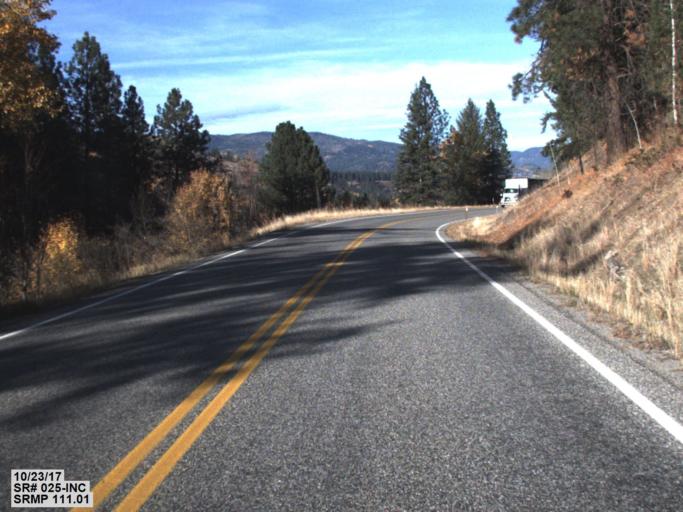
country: CA
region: British Columbia
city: Rossland
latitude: 48.8943
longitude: -117.8178
